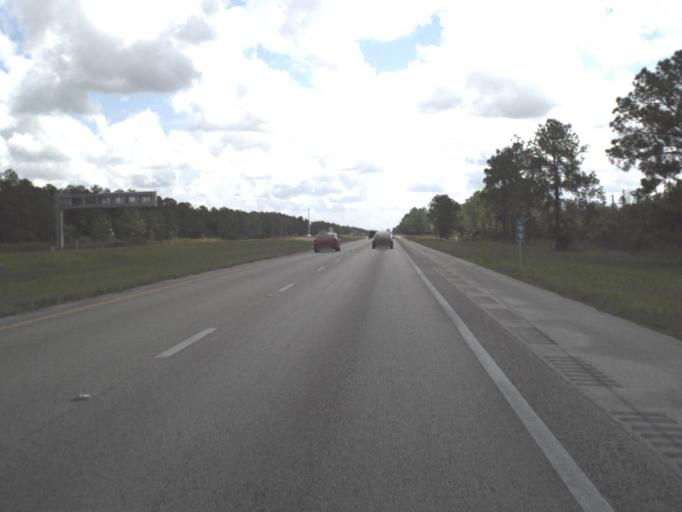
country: US
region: Florida
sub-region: Collier County
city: Golden Gate
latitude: 26.1548
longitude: -81.6484
